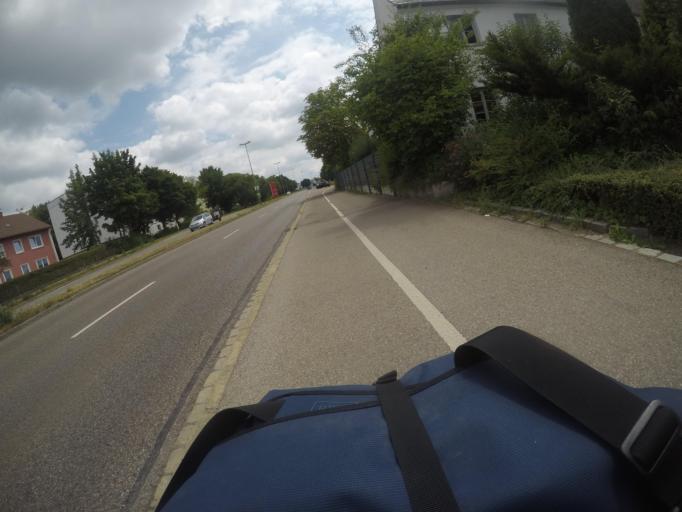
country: DE
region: Bavaria
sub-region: Swabia
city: Memmingen
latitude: 48.0010
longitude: 10.1753
